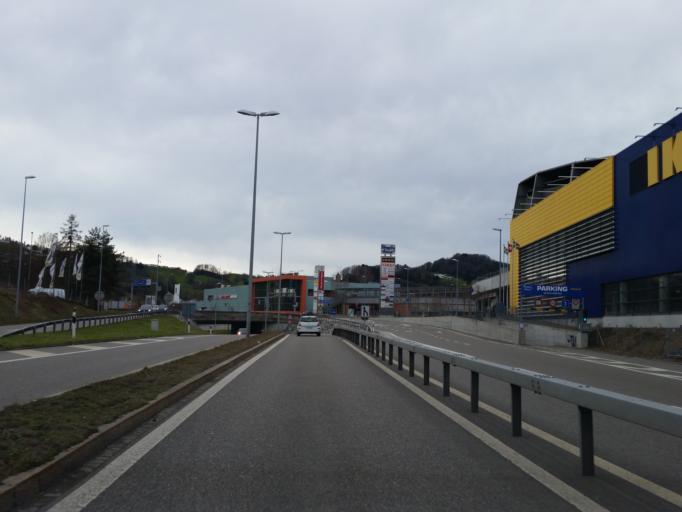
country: CH
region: Appenzell Ausserrhoden
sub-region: Bezirk Hinterland
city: Herisau
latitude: 47.4088
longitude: 9.3085
